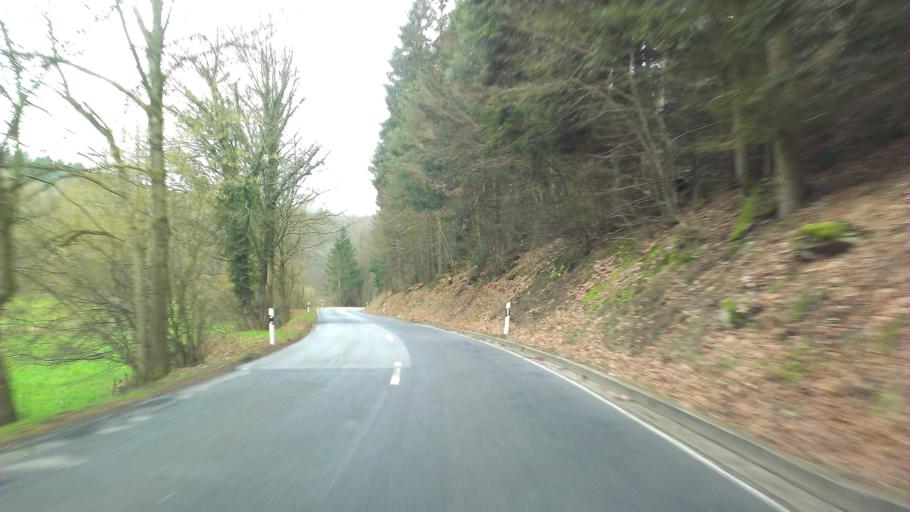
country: DE
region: Baden-Wuerttemberg
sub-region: Karlsruhe Region
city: Heiligkreuzsteinach
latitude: 49.4953
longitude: 8.7828
